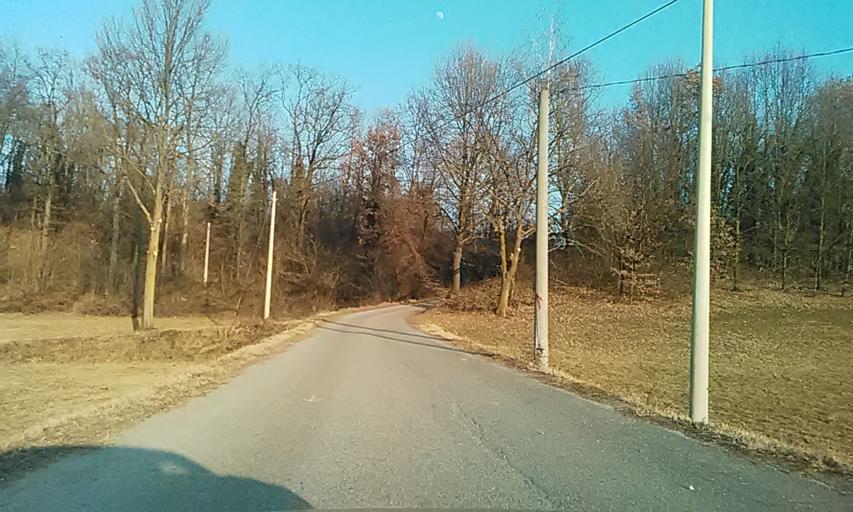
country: IT
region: Piedmont
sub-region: Provincia di Biella
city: Dorzano
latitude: 45.4168
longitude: 8.1108
